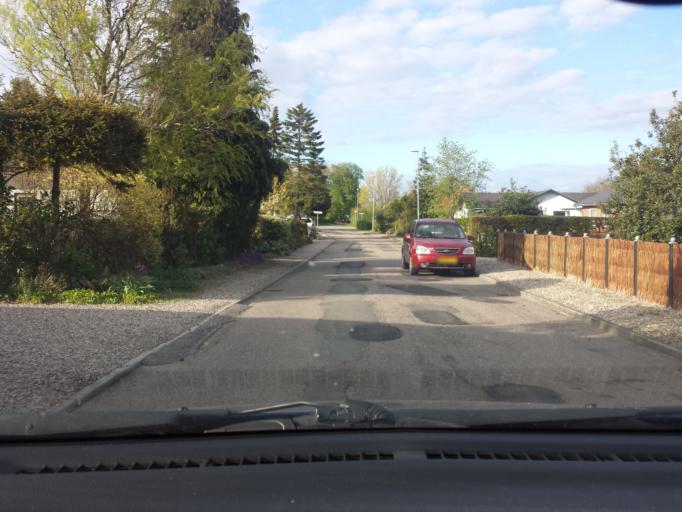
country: DK
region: South Denmark
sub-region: Langeland Kommune
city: Rudkobing
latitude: 54.8608
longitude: 10.7288
